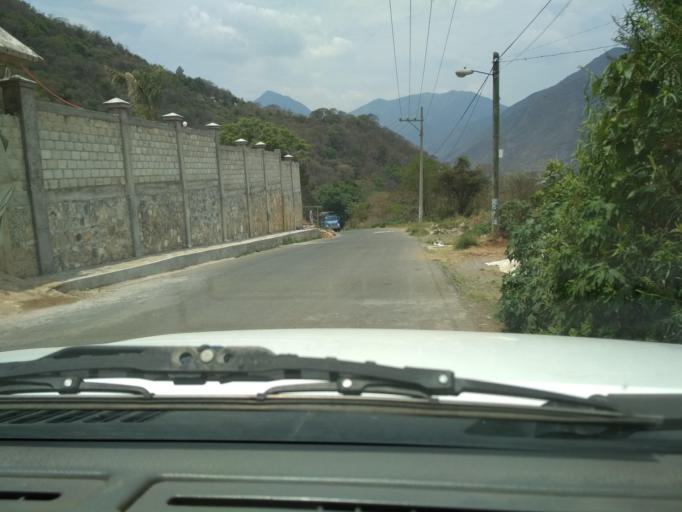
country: MX
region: Veracruz
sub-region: Camerino Z. Mendoza
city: La Cuesta
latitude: 18.7941
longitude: -97.1770
